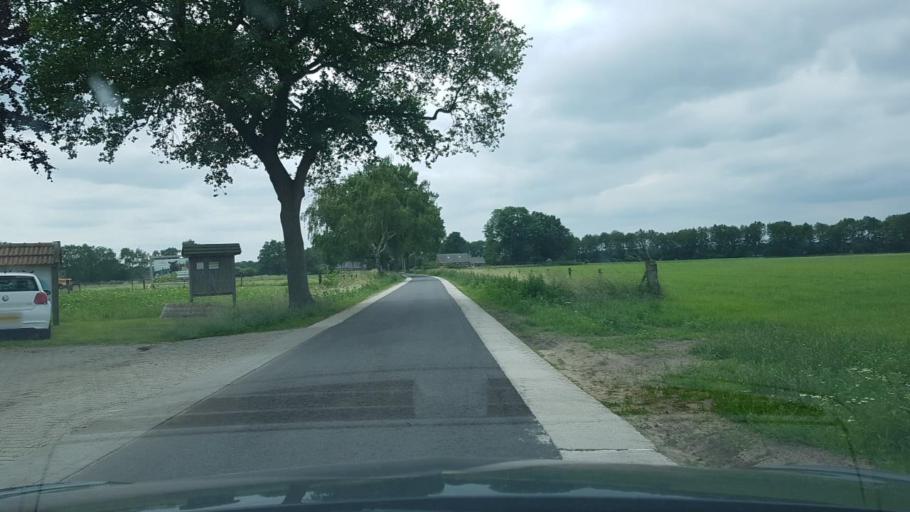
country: NL
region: Overijssel
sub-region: Gemeente Raalte
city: Raalte
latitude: 52.3513
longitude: 6.3769
